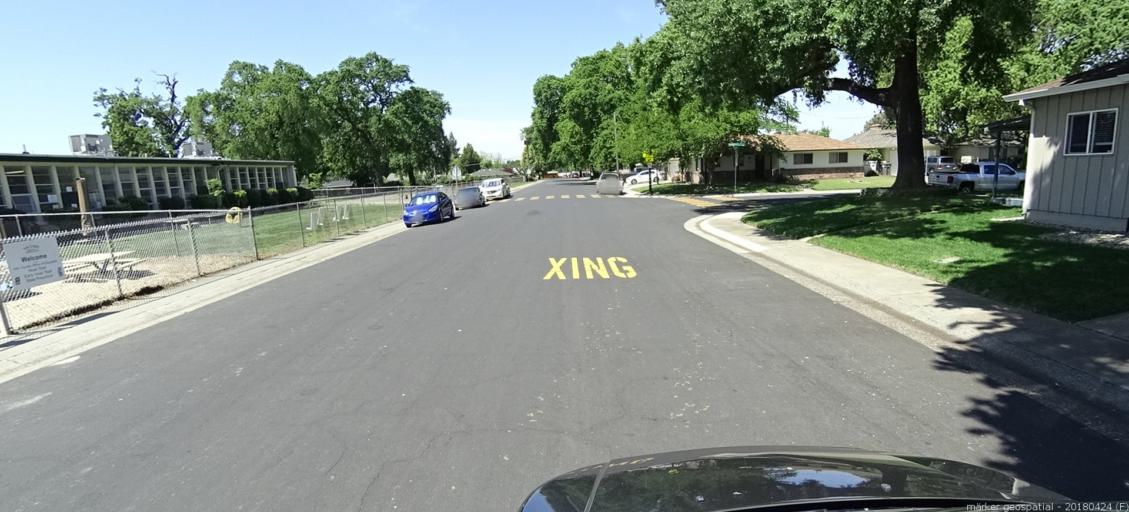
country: US
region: California
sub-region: Yolo County
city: West Sacramento
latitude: 38.5710
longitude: -121.5337
